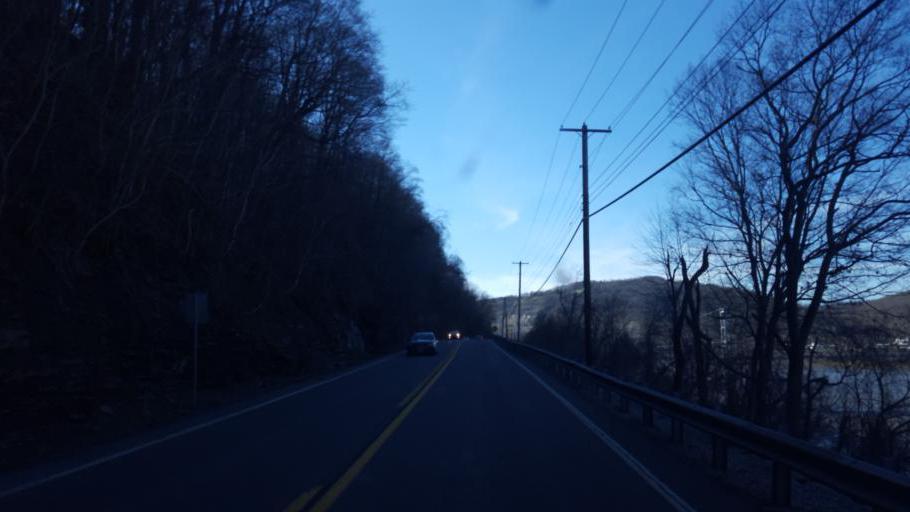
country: US
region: Ohio
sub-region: Columbiana County
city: East Liverpool
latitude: 40.6160
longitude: -80.5892
